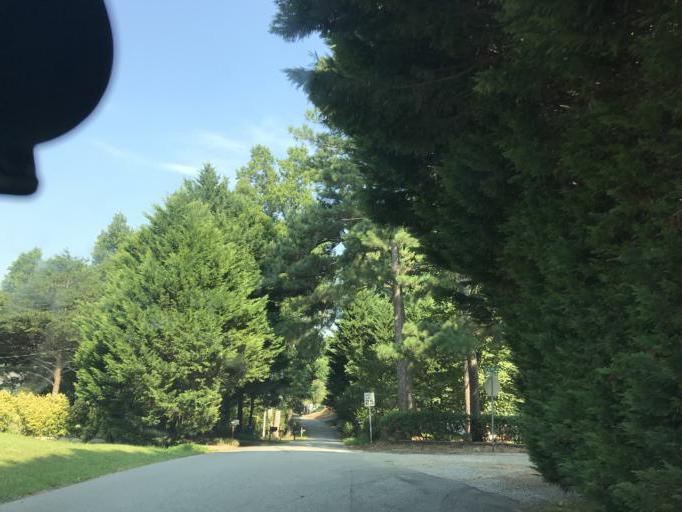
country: US
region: Georgia
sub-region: Forsyth County
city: Cumming
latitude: 34.2225
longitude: -84.0861
